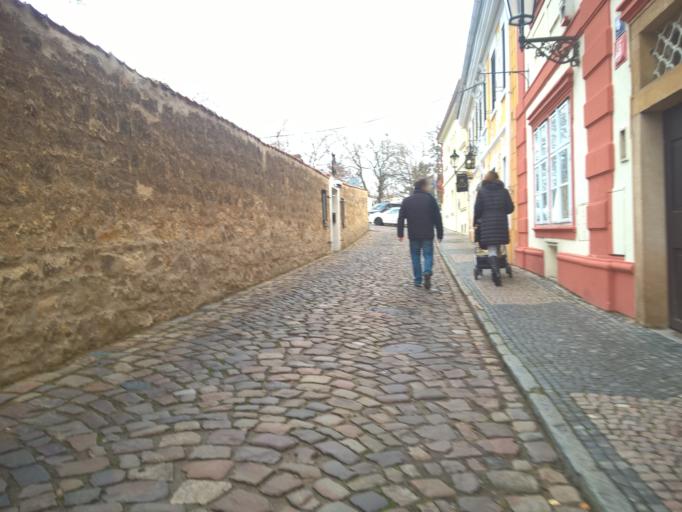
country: CZ
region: Praha
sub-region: Praha 1
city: Mala Strana
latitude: 50.0907
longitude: 14.3925
